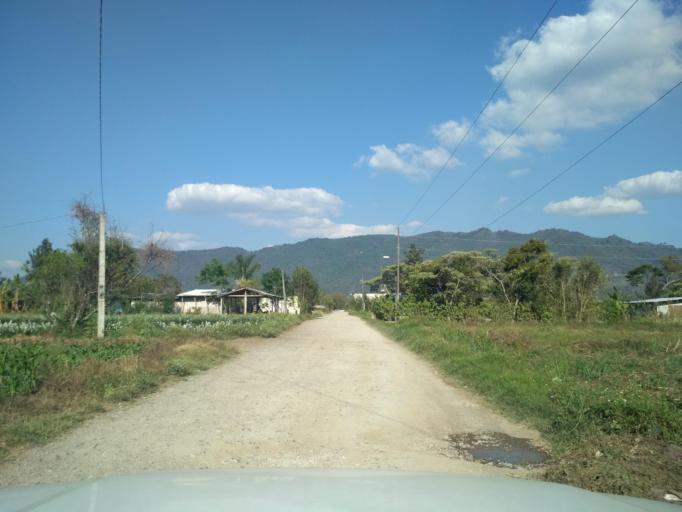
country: MX
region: Veracruz
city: Jalapilla
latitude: 18.8093
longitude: -97.0914
